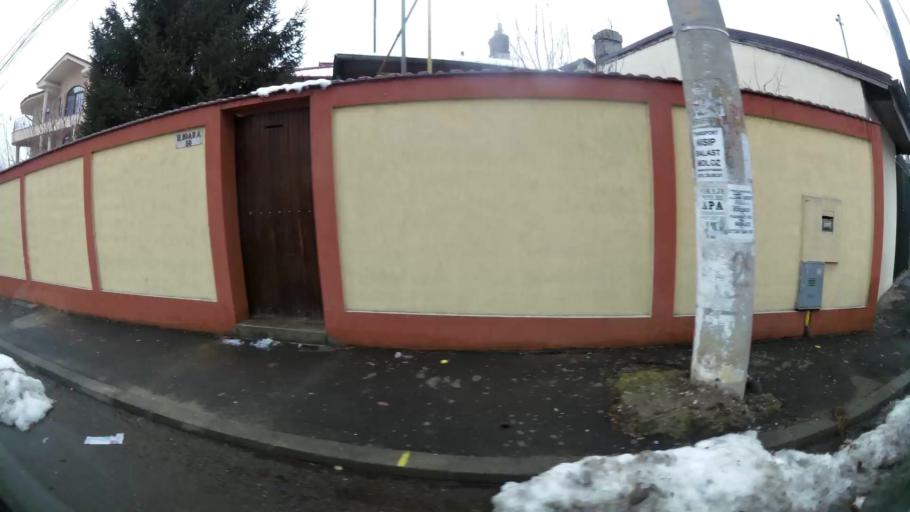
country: RO
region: Ilfov
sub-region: Comuna Popesti-Leordeni
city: Popesti-Leordeni
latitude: 44.4077
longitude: 26.1630
